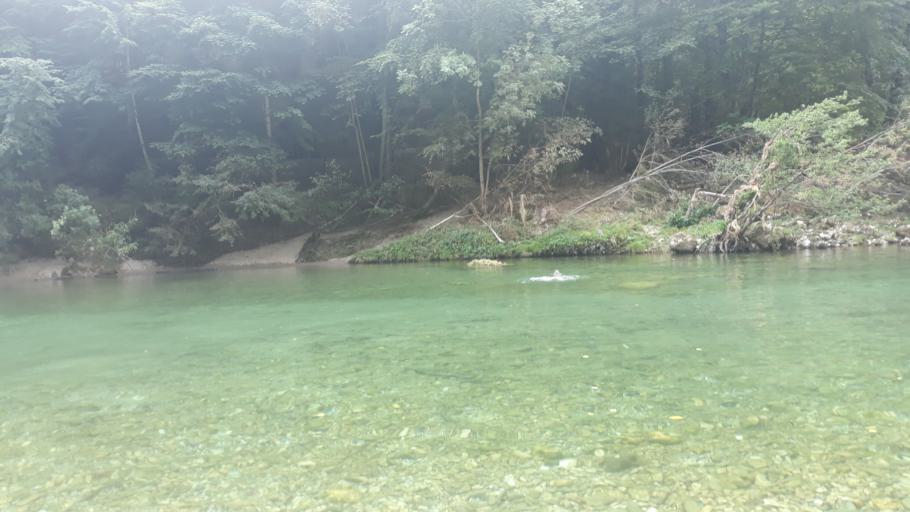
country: FR
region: Languedoc-Roussillon
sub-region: Departement de la Lozere
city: La Canourgue
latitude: 44.3054
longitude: 3.2562
